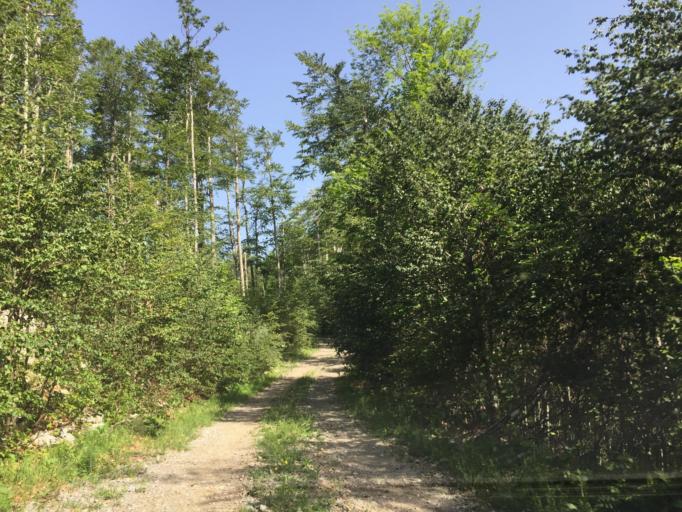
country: HR
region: Primorsko-Goranska
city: Krasica
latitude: 45.4174
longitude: 14.5906
